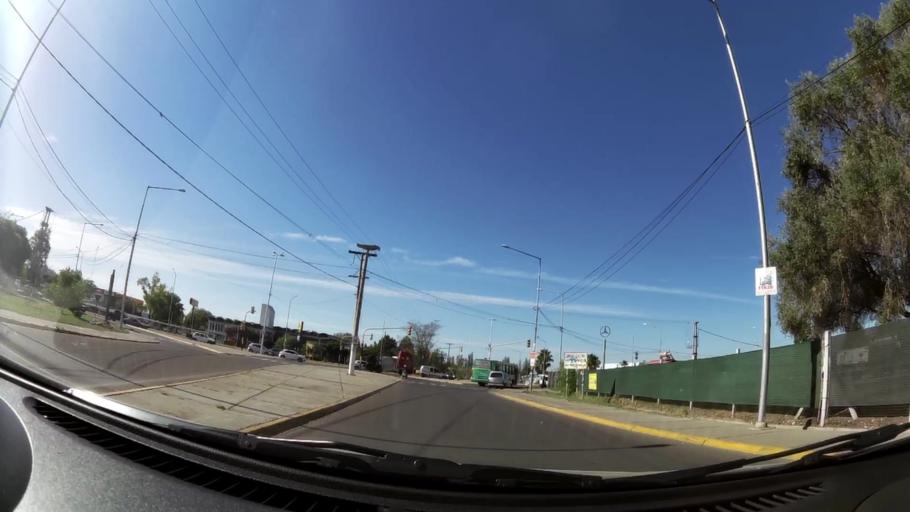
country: AR
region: Mendoza
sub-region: Departamento de Godoy Cruz
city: Godoy Cruz
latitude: -32.9326
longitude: -68.7985
